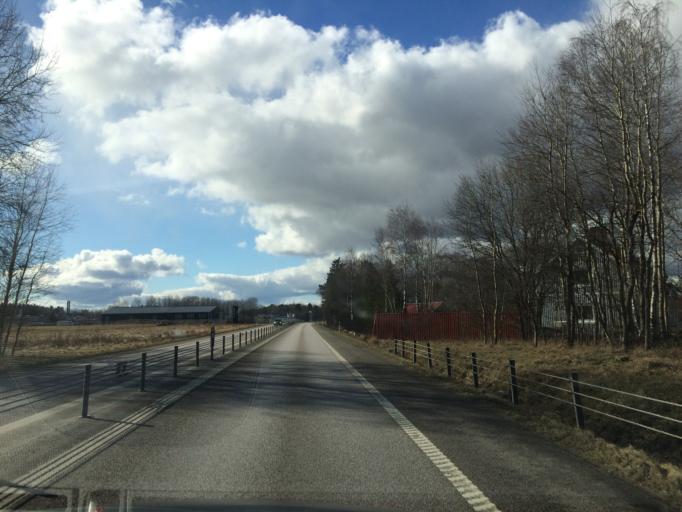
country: SE
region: Vaestra Goetaland
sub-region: Skara Kommun
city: Skara
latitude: 58.3758
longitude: 13.4337
